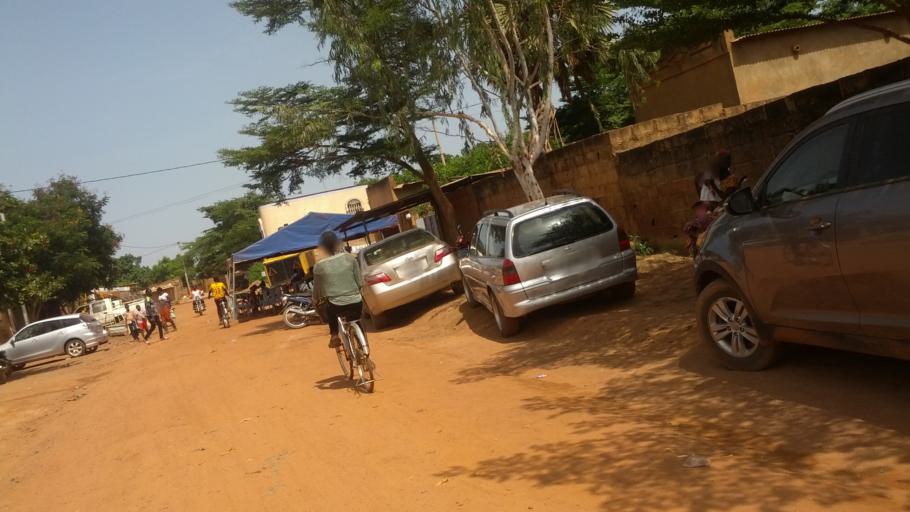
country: BF
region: Centre
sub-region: Kadiogo Province
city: Ouagadougou
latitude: 12.3856
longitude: -1.4661
